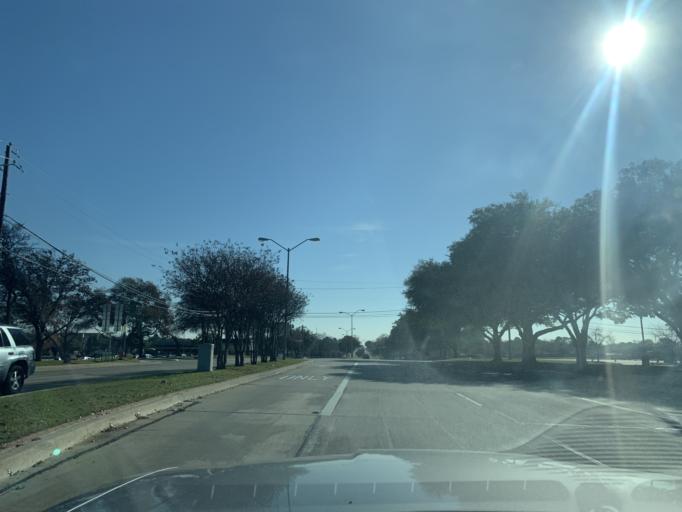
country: US
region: Texas
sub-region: Tarrant County
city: Bedford
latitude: 32.8354
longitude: -97.1335
